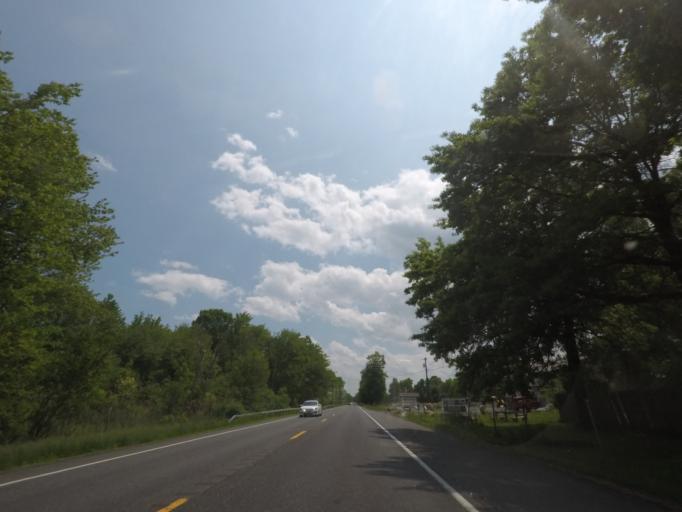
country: US
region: New York
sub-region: Columbia County
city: Kinderhook
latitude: 42.3434
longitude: -73.7048
